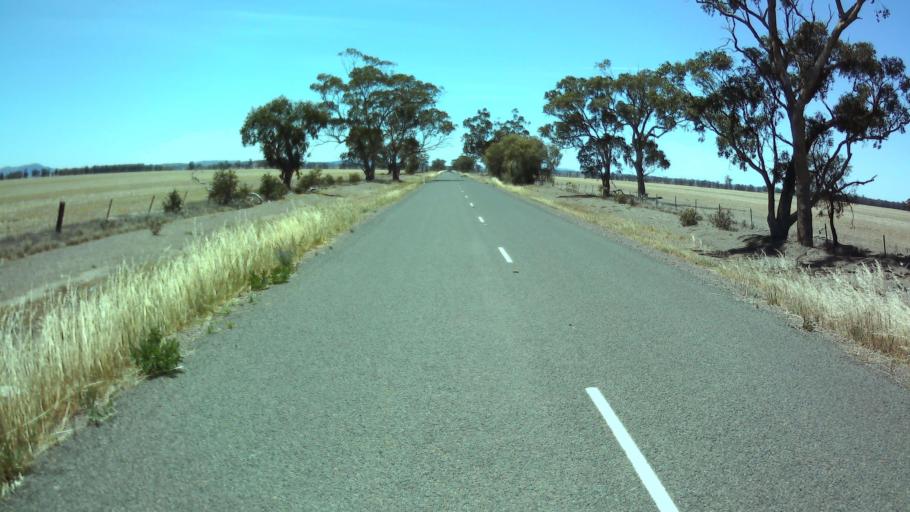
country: AU
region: New South Wales
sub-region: Bland
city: West Wyalong
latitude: -33.6583
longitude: 147.5807
